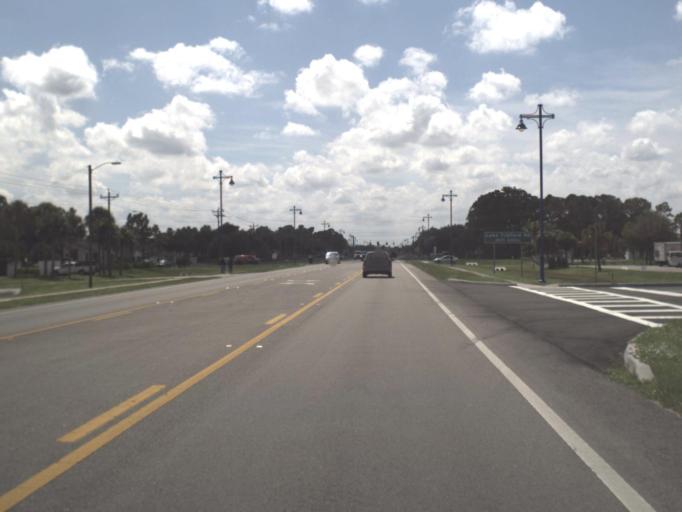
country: US
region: Florida
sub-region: Collier County
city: Immokalee
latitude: 26.4373
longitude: -81.4339
